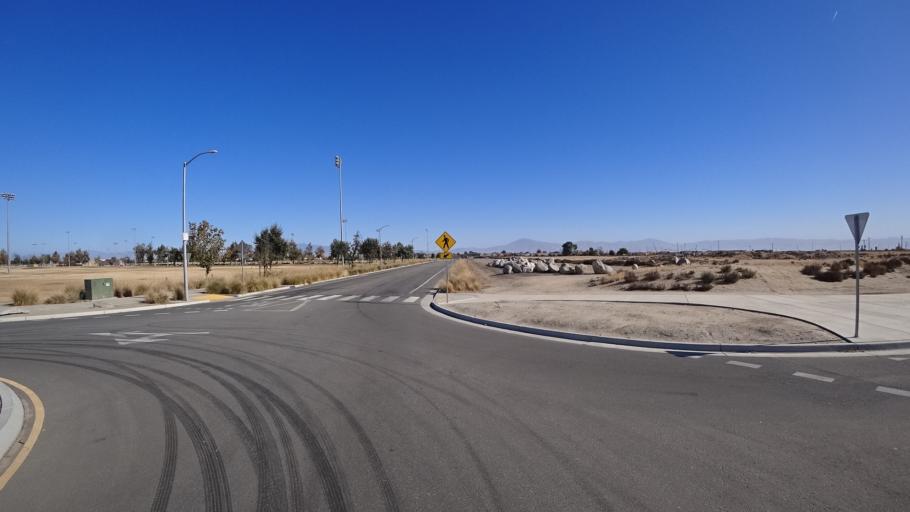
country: US
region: California
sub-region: Kern County
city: Greenfield
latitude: 35.2696
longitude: -119.0793
